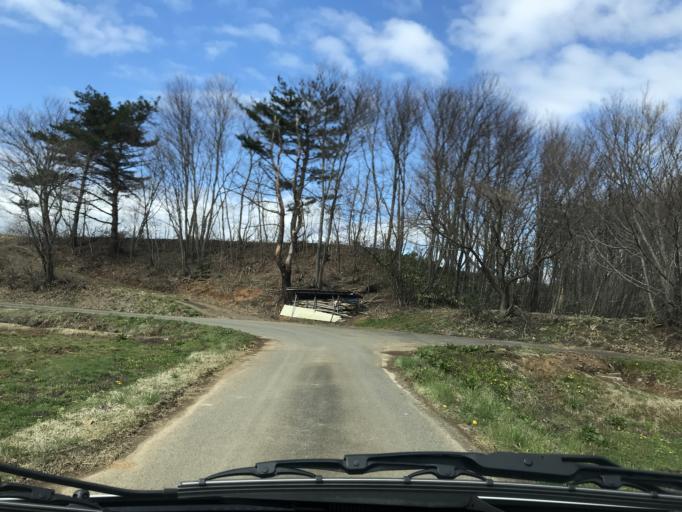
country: JP
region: Iwate
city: Mizusawa
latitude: 39.0789
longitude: 140.9892
